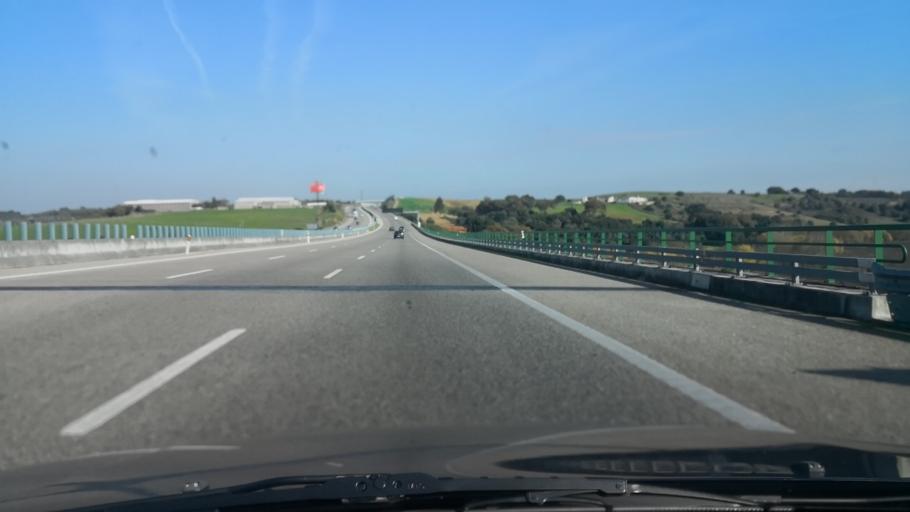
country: PT
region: Santarem
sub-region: Alcanena
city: Alcanena
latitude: 39.3517
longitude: -8.6449
